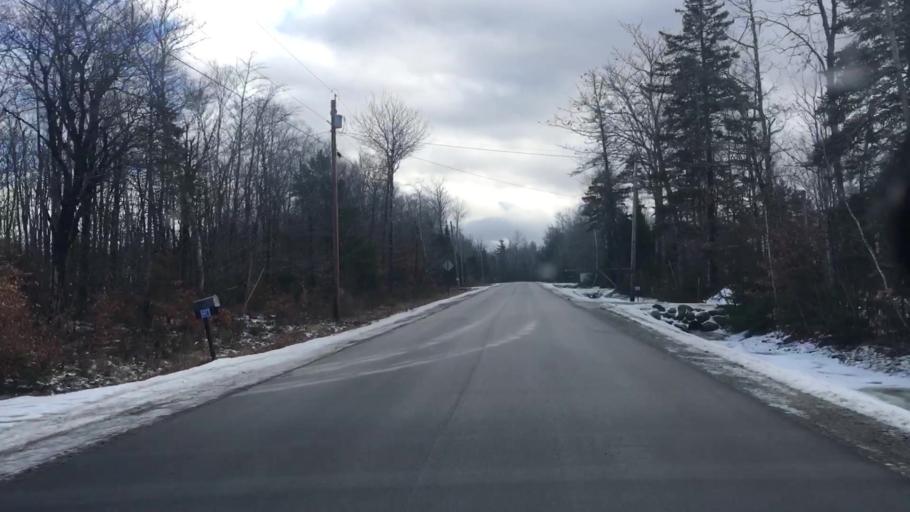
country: US
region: Maine
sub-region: Hancock County
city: Dedham
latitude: 44.6821
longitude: -68.7078
